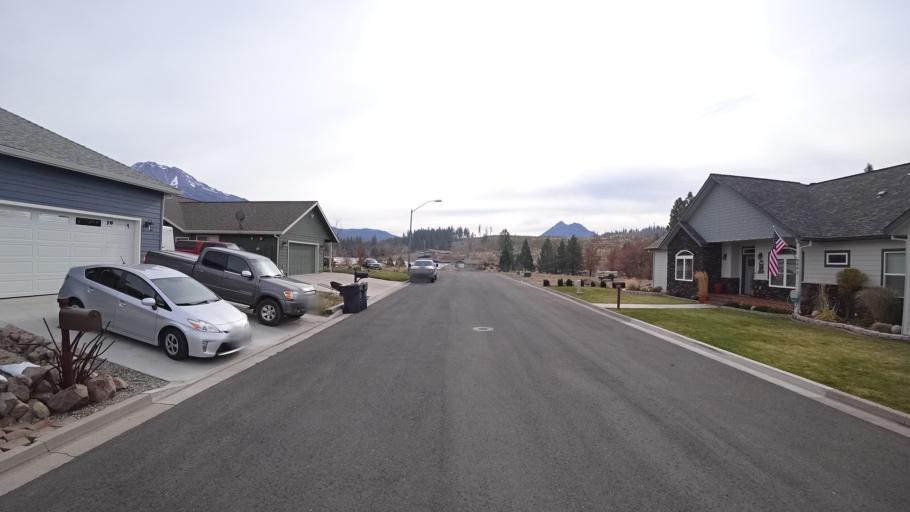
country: US
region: California
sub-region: Siskiyou County
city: Weed
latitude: 41.4298
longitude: -122.3796
